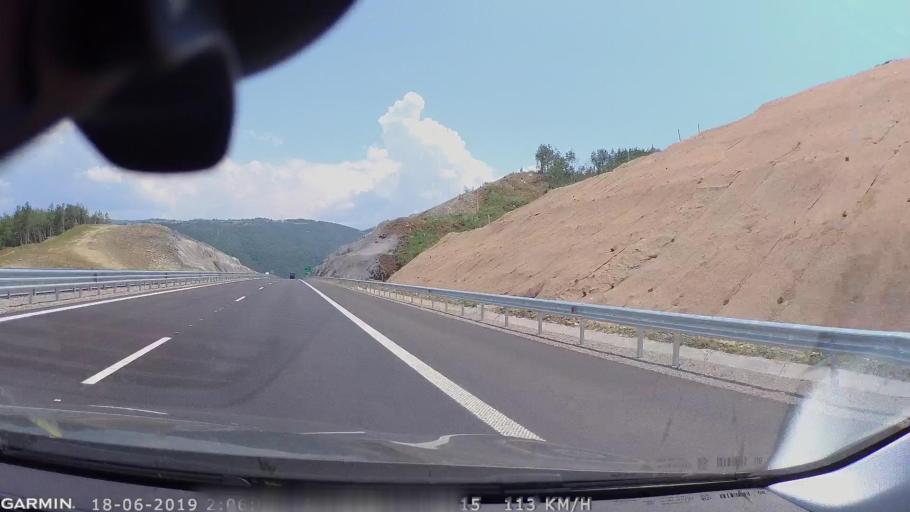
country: BG
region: Blagoevgrad
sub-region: Obshtina Blagoevgrad
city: Blagoevgrad
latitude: 41.9704
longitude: 23.0848
